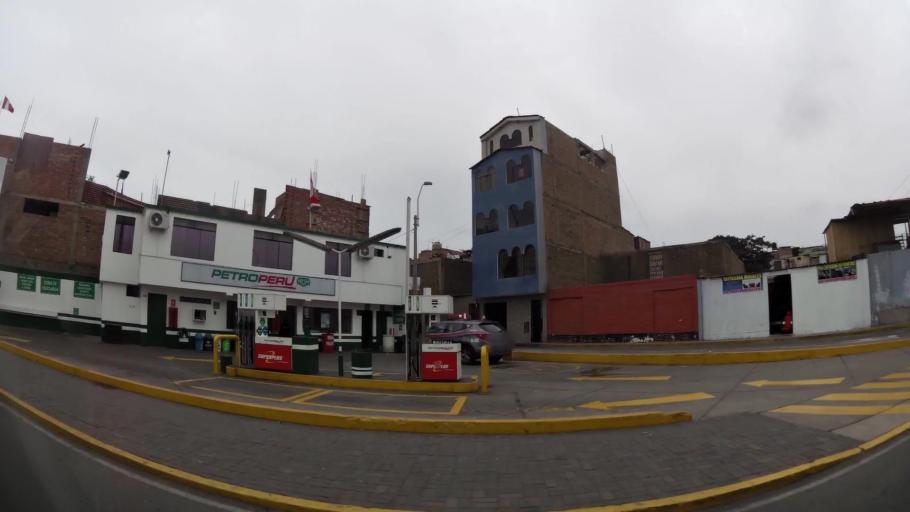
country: PE
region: Lima
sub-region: Lima
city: Surco
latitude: -12.1467
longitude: -77.0093
